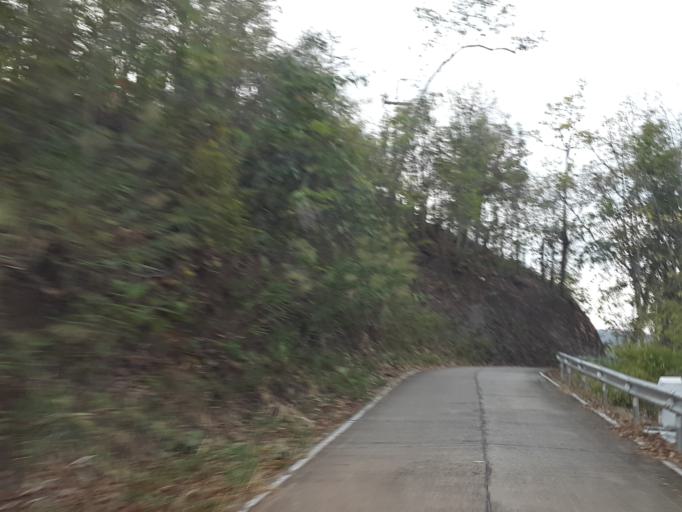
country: TH
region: Lampang
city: Mueang Pan
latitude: 18.8149
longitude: 99.4739
